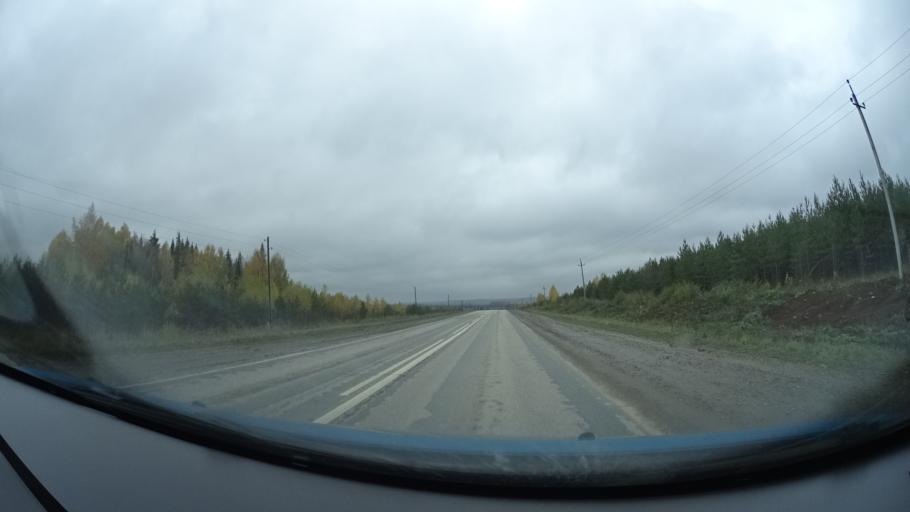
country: RU
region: Perm
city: Osa
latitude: 57.1202
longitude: 55.5232
